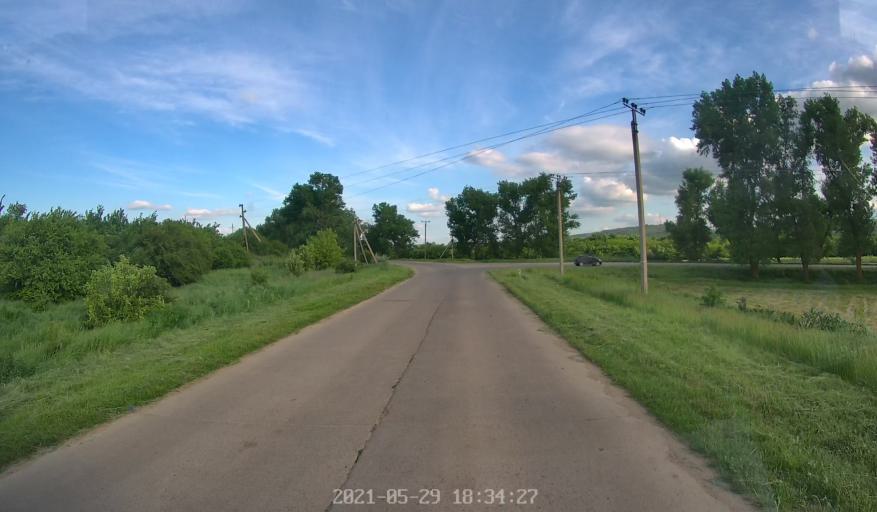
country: MD
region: Chisinau
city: Singera
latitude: 46.8131
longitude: 28.9128
